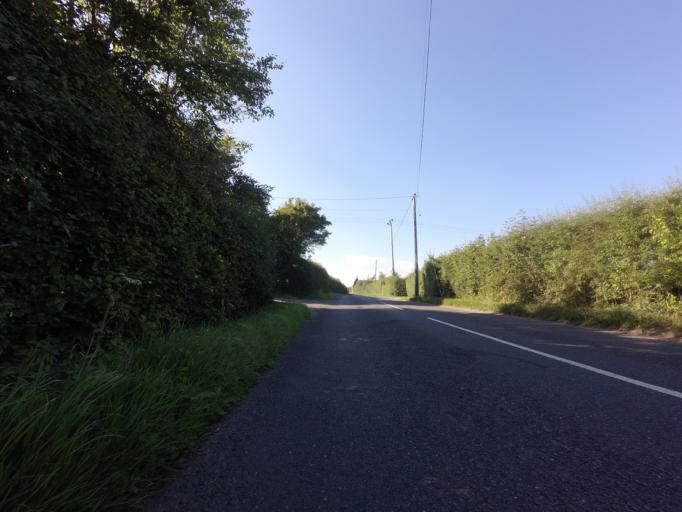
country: GB
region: England
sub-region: Kent
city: Tenterden
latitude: 51.0510
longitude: 0.6939
